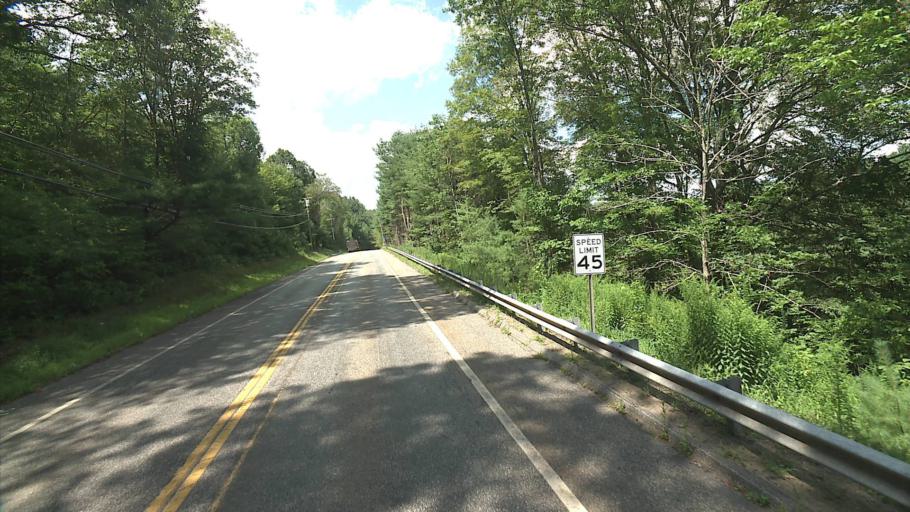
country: US
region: Connecticut
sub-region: Tolland County
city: Storrs
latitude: 41.8768
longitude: -72.1613
